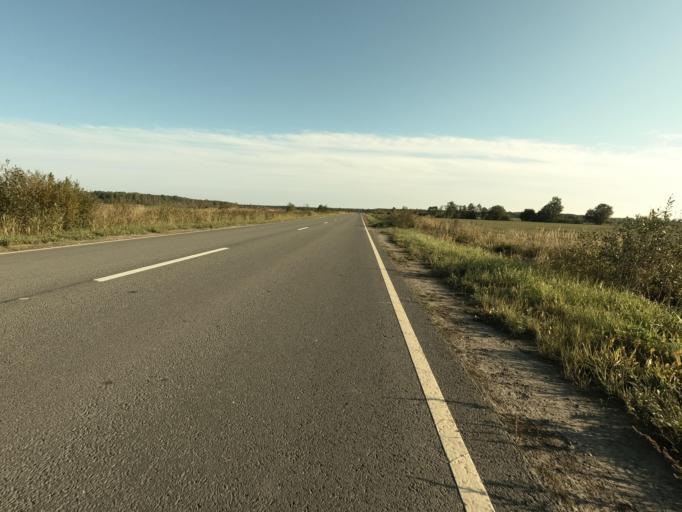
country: RU
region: St.-Petersburg
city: Sapernyy
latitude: 59.7396
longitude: 30.6519
